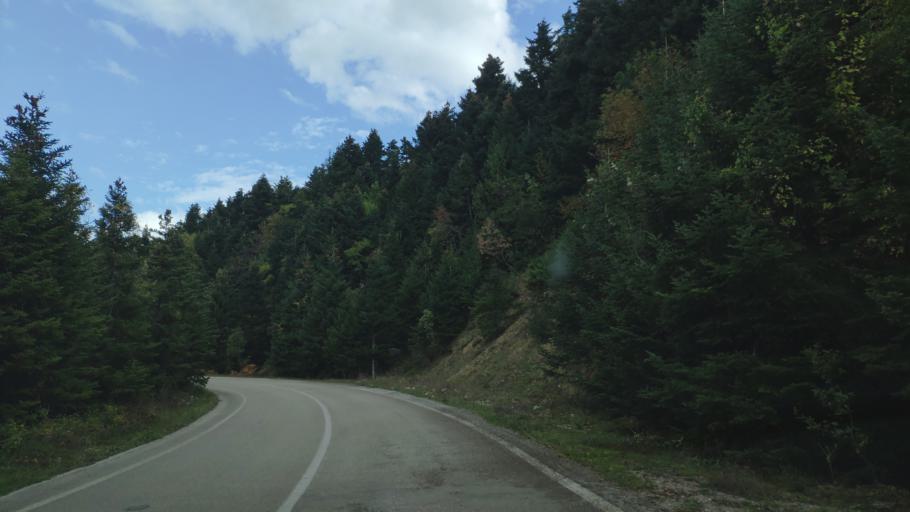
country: GR
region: Central Greece
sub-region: Nomos Fthiotidos
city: Stavros
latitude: 38.7311
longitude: 22.3625
